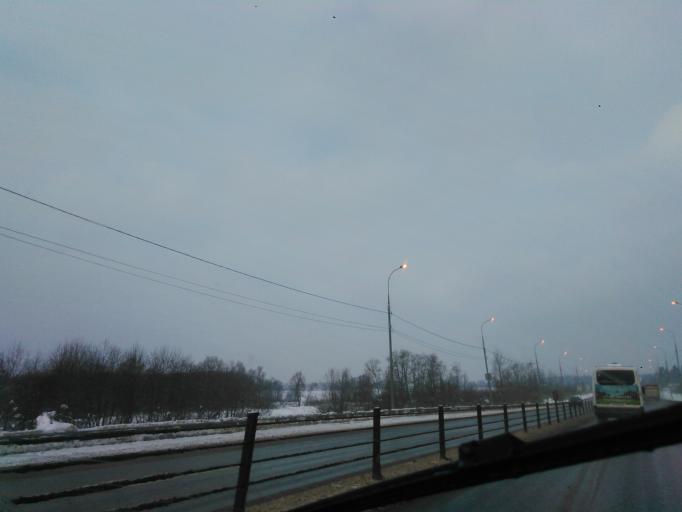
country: RU
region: Moskovskaya
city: Podosinki
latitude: 56.2143
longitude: 37.5217
